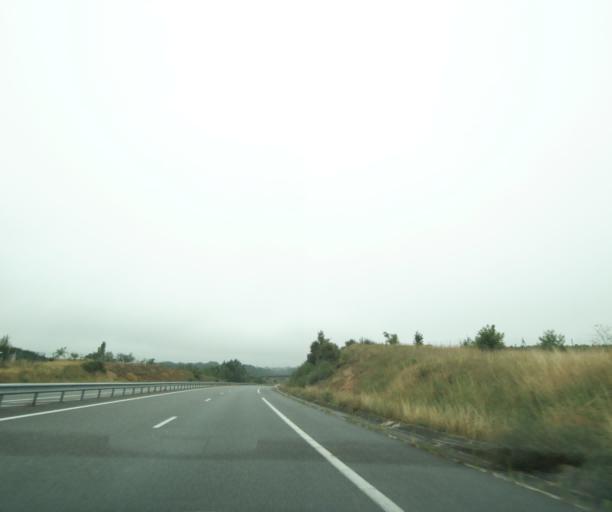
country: FR
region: Midi-Pyrenees
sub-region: Departement du Tarn
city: Carmaux
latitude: 44.0627
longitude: 2.2156
